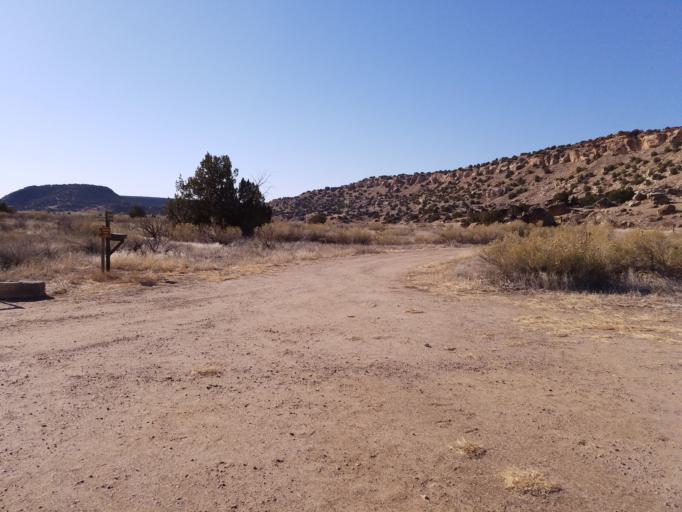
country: US
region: Colorado
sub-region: Otero County
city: La Junta
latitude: 37.6200
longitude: -103.5992
